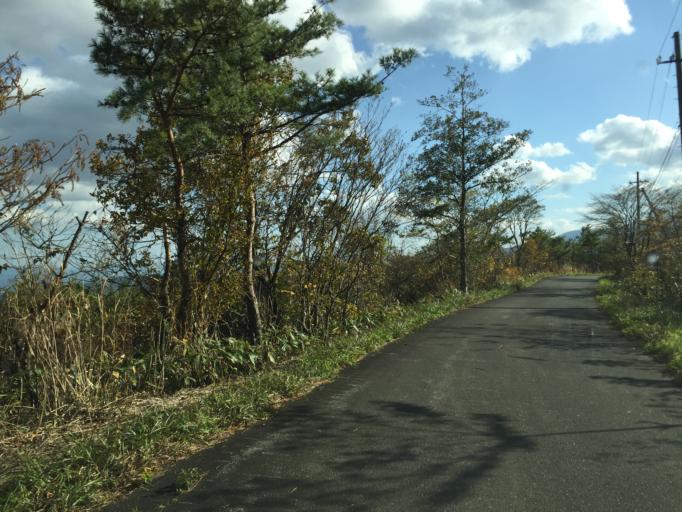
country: JP
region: Fukushima
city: Fukushima-shi
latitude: 37.7292
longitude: 140.3153
